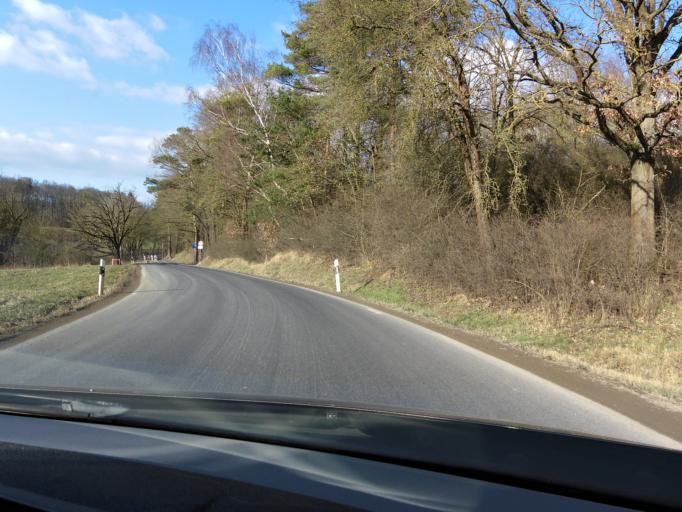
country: DE
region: Thuringia
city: Leimbach
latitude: 50.8353
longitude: 10.2058
